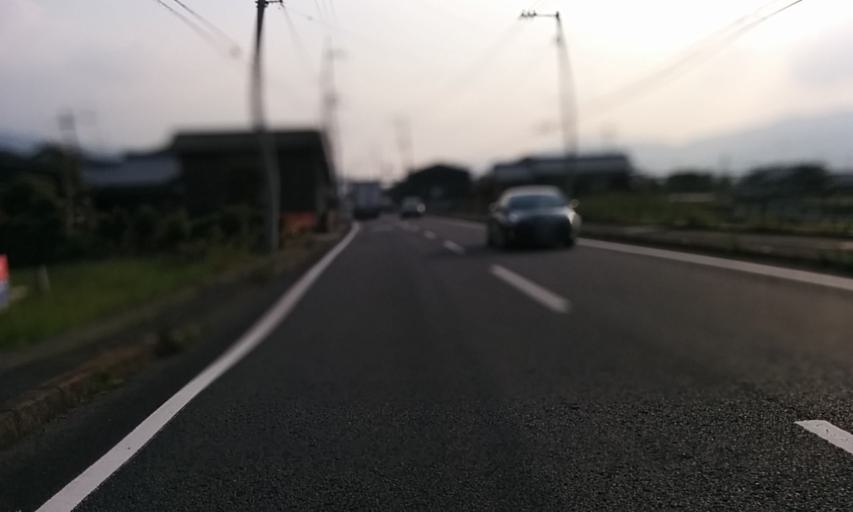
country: JP
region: Ehime
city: Saijo
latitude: 33.8938
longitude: 133.0934
